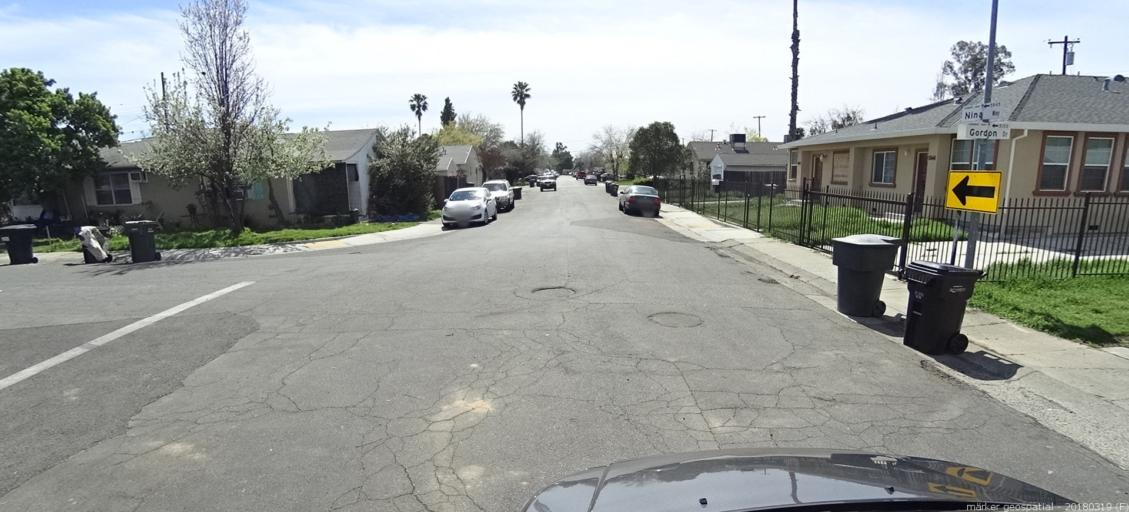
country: US
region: California
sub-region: Sacramento County
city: Parkway
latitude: 38.5209
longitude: -121.4457
